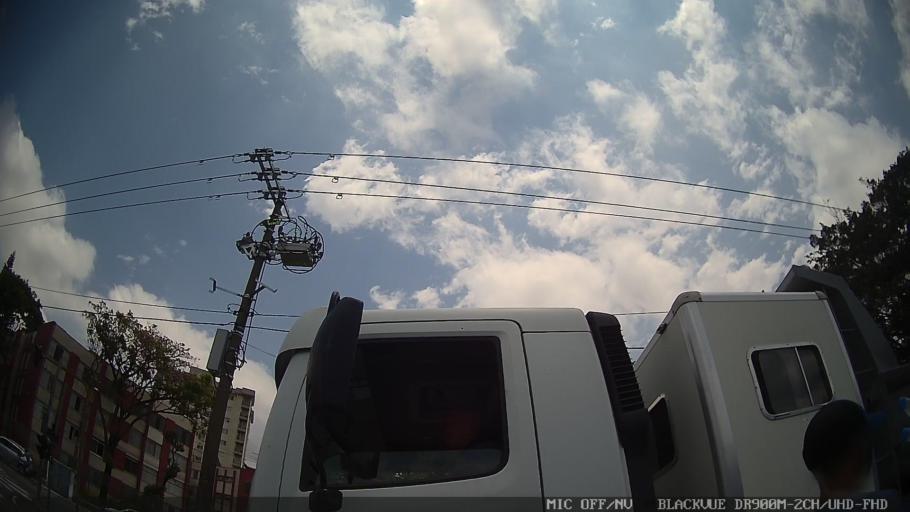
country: BR
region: Sao Paulo
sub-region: Osasco
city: Osasco
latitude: -23.4896
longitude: -46.7104
